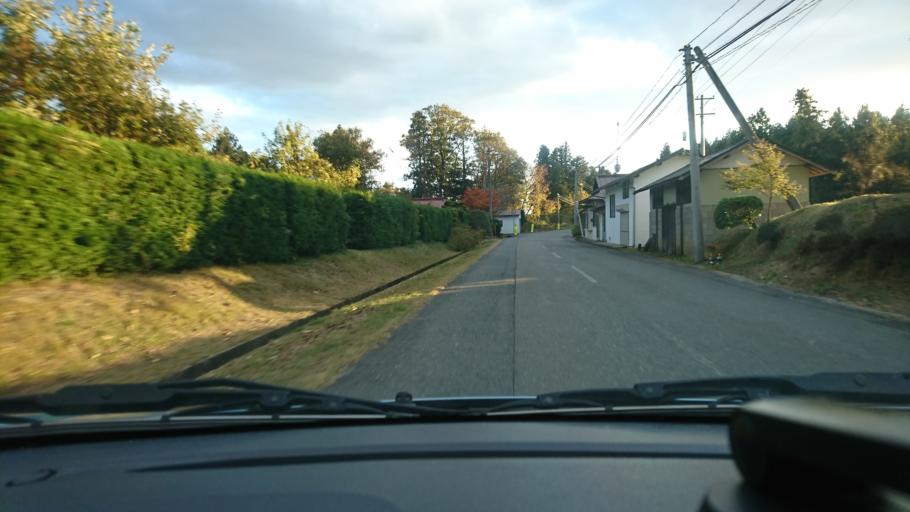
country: JP
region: Iwate
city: Ichinoseki
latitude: 38.7946
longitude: 141.1924
